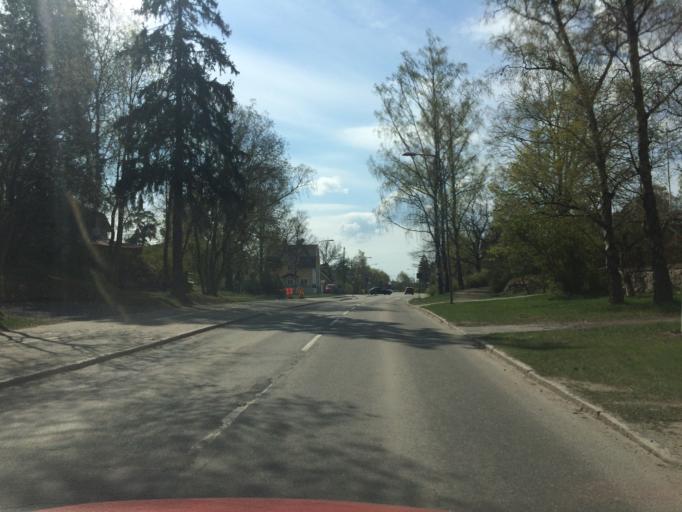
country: SE
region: Stockholm
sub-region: Huddinge Kommun
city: Segeltorp
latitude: 59.2955
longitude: 17.9552
